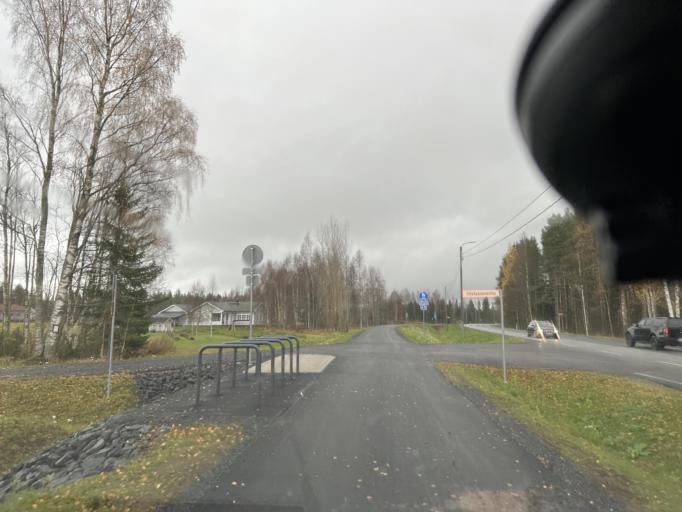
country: FI
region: Northern Ostrobothnia
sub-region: Ylivieska
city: Sievi
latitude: 63.9450
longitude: 24.5281
